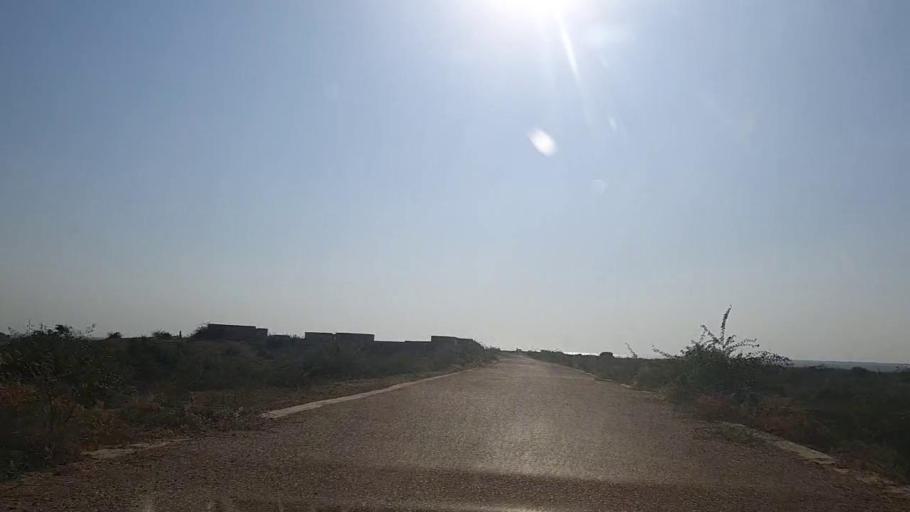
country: PK
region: Sindh
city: Daro Mehar
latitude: 25.0053
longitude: 68.1149
